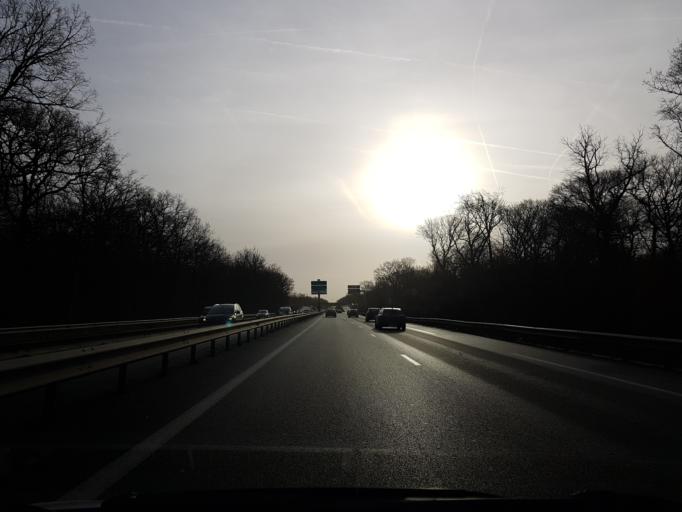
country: FR
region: Ile-de-France
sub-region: Departement de l'Essonne
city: Tigery
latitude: 48.6645
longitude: 2.5131
